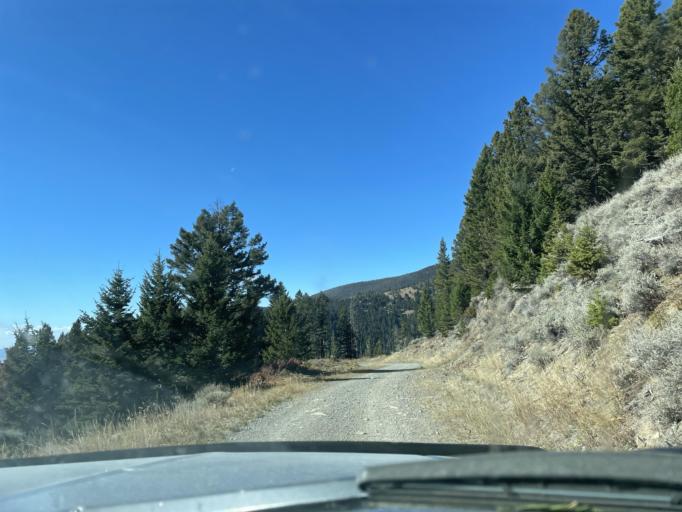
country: US
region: Montana
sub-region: Broadwater County
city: Townsend
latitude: 46.5093
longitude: -111.2840
